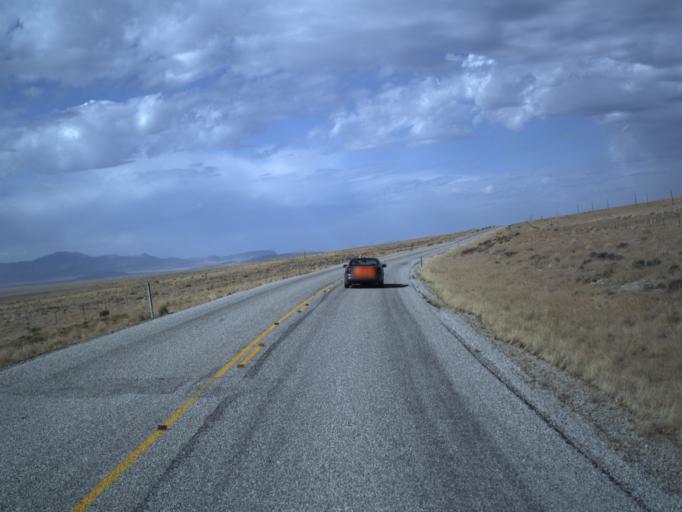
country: US
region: Utah
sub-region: Tooele County
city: Wendover
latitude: 41.4422
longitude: -113.6937
